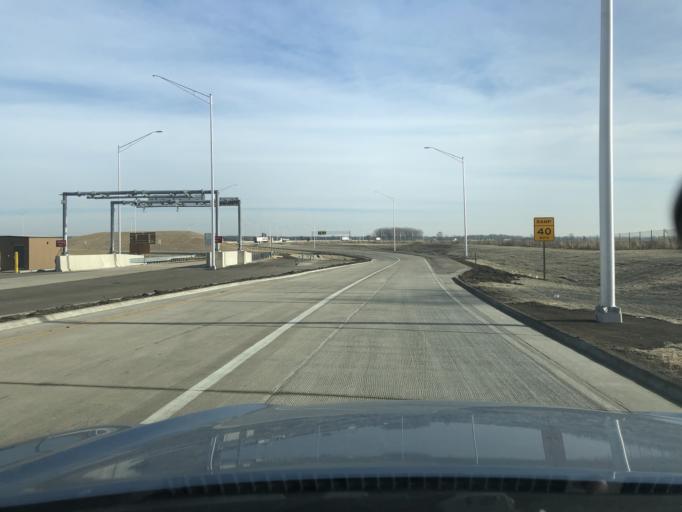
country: US
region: Illinois
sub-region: McHenry County
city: Marengo
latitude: 42.1751
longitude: -88.6172
